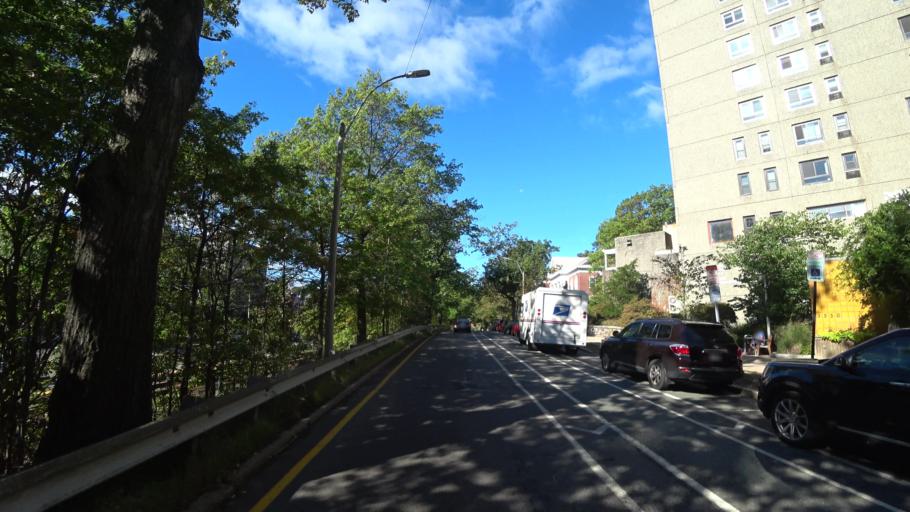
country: US
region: Massachusetts
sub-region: Norfolk County
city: Brookline
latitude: 42.3398
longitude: -71.1315
